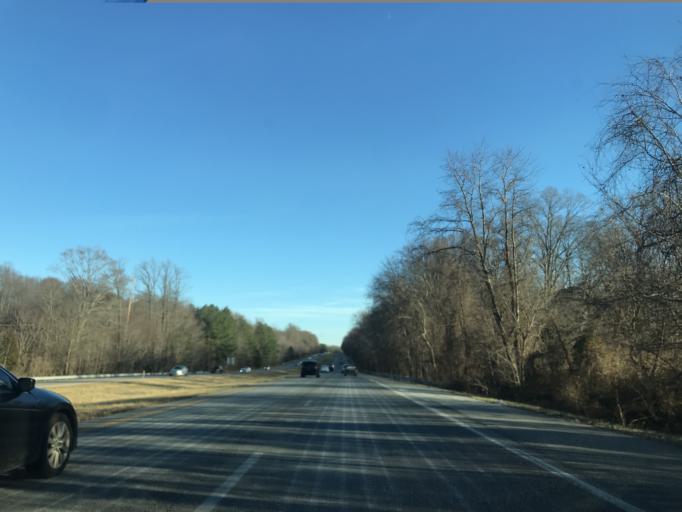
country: US
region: Maryland
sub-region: Prince George's County
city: Marlboro Meadows
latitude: 38.8007
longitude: -76.6851
